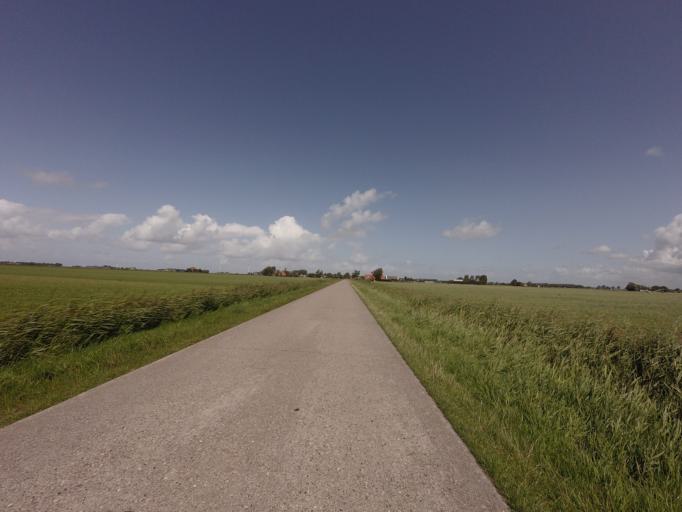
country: NL
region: Friesland
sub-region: Sudwest Fryslan
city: Makkum
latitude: 53.0730
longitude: 5.4536
